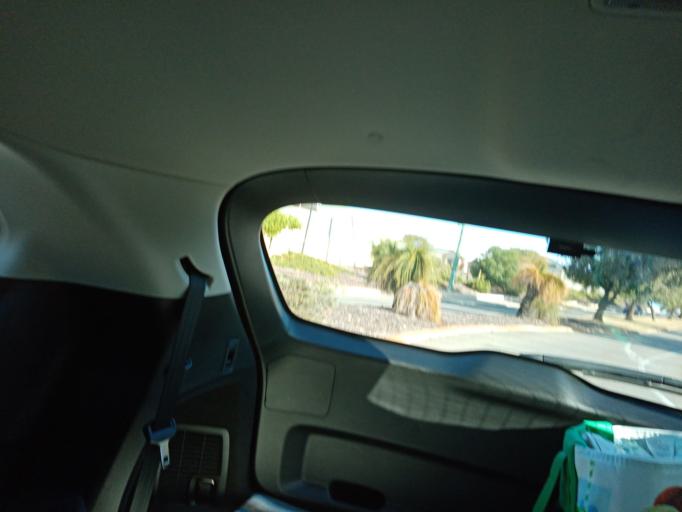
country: AU
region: Western Australia
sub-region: City of Cockburn
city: Beeliar
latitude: -32.1312
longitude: 115.8116
